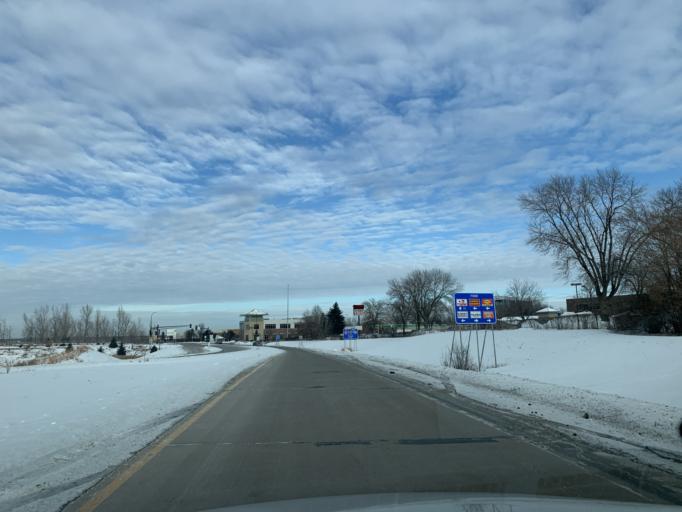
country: US
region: Minnesota
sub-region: Dakota County
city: Burnsville
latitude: 44.7679
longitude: -93.2877
